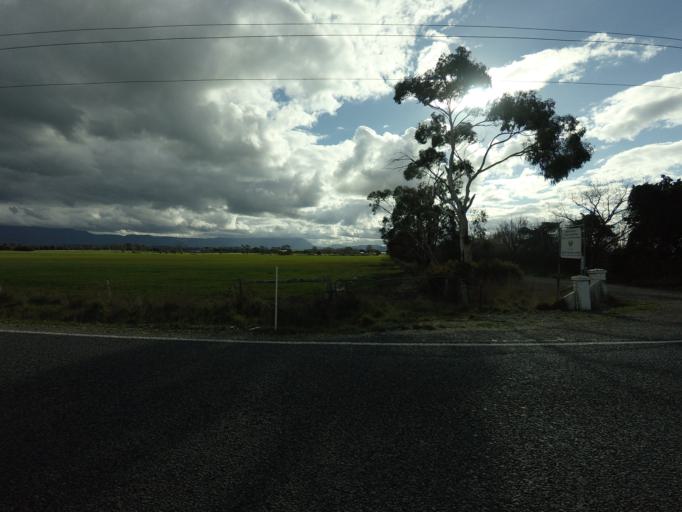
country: AU
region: Tasmania
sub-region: Northern Midlands
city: Longford
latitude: -41.7243
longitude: 147.0891
